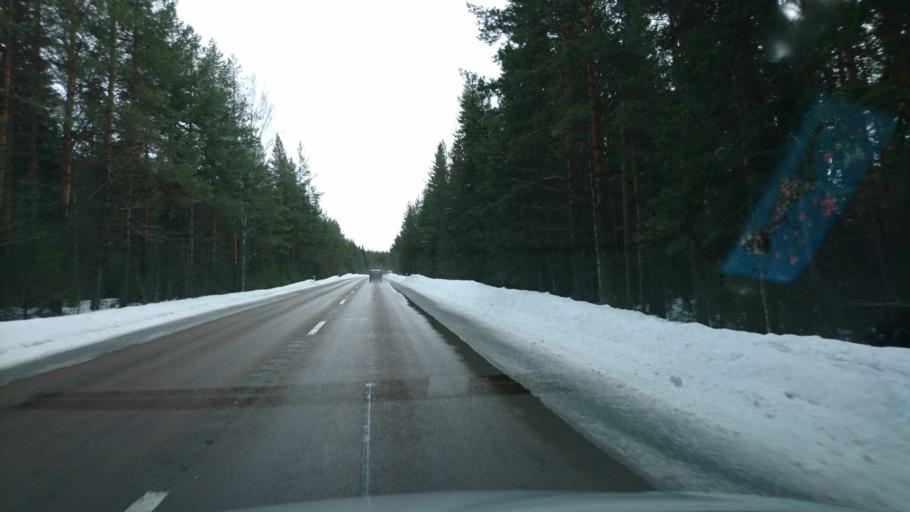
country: SE
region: Vaesternorrland
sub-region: Solleftea Kommun
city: Solleftea
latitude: 63.1047
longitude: 17.0095
